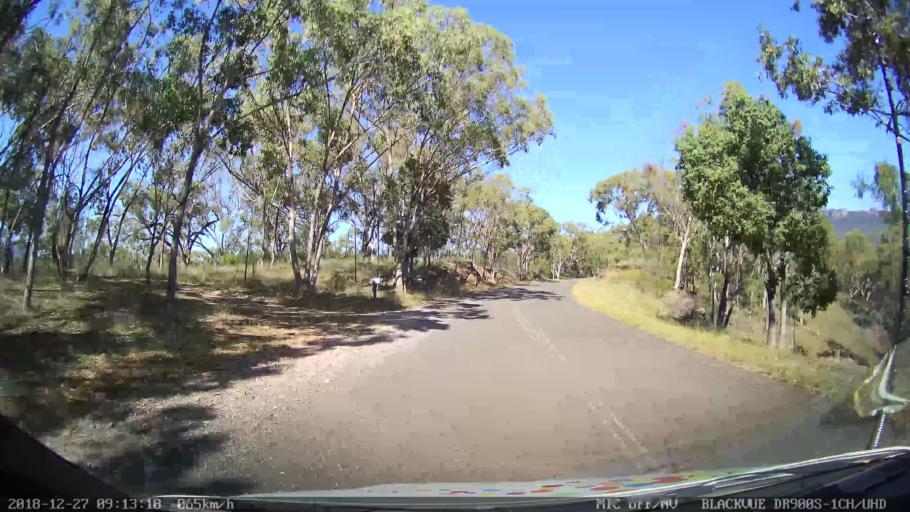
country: AU
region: New South Wales
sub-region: Lithgow
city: Portland
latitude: -33.1381
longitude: 150.0956
